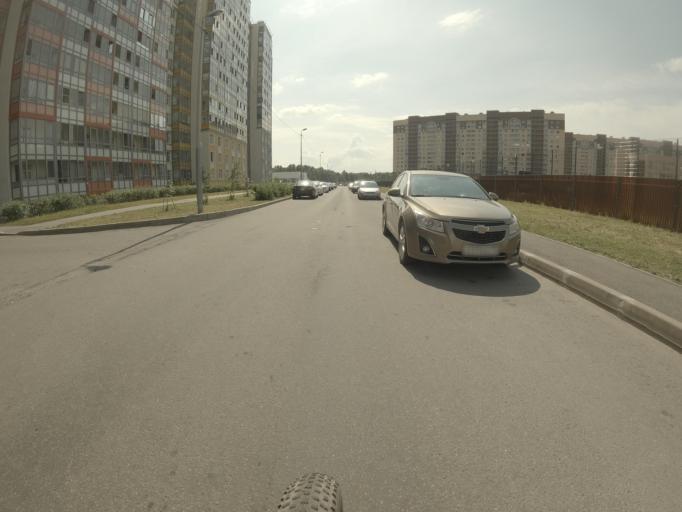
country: RU
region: St.-Petersburg
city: Krasnogvargeisky
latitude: 59.9163
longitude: 30.4384
